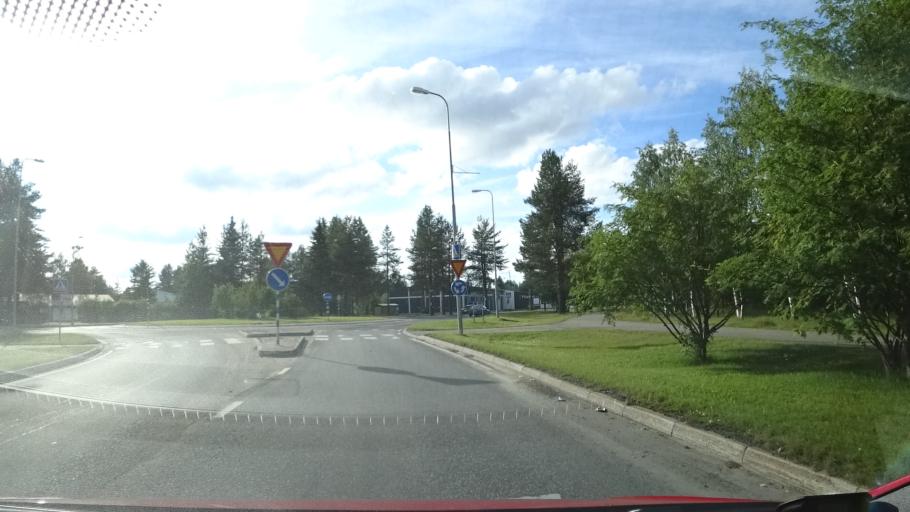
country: FI
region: Lapland
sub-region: Pohjois-Lappi
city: Sodankylae
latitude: 67.4211
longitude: 26.5892
